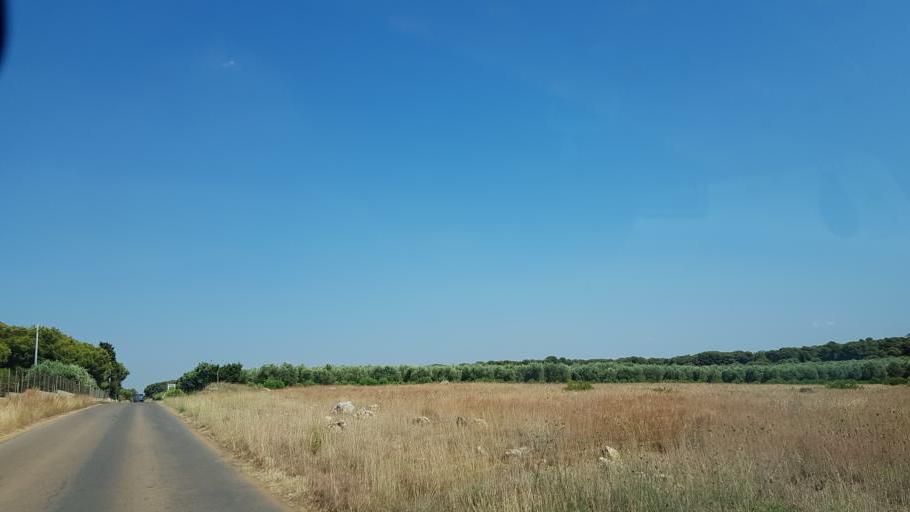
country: IT
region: Apulia
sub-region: Provincia di Lecce
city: Nardo
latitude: 40.1742
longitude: 17.9497
